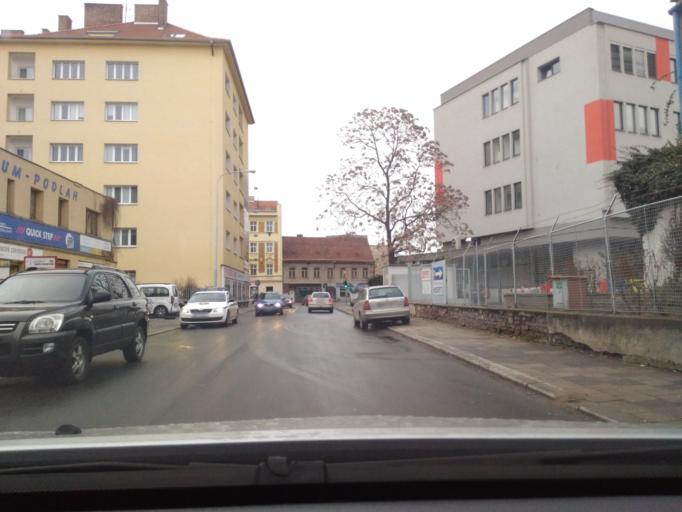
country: CZ
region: South Moravian
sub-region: Mesto Brno
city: Brno
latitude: 49.1905
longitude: 16.6214
